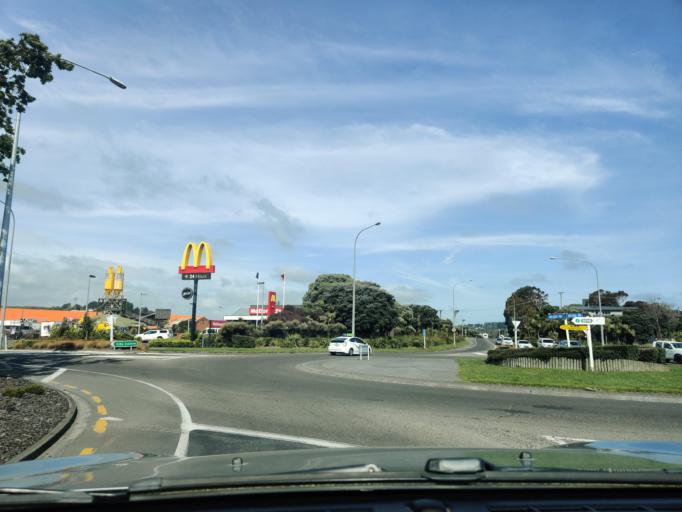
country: NZ
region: Manawatu-Wanganui
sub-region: Wanganui District
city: Wanganui
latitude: -39.9413
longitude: 175.0419
